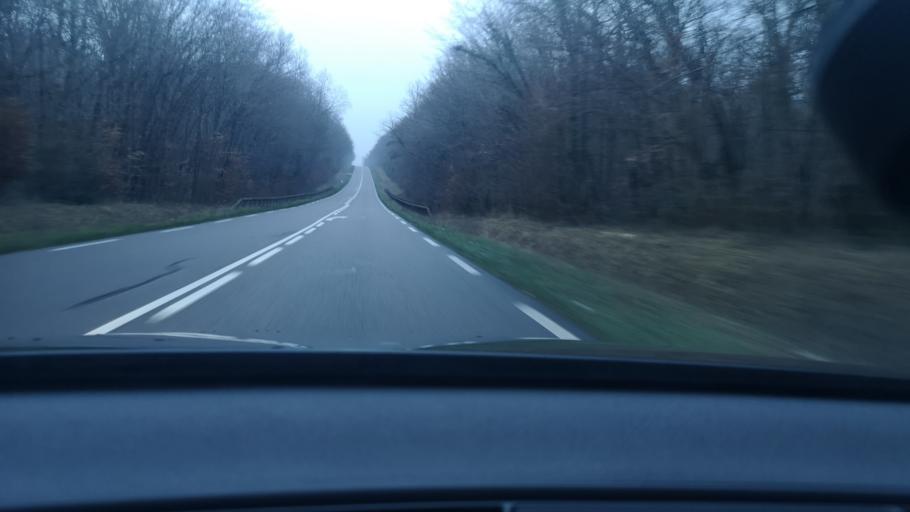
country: FR
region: Bourgogne
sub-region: Departement de la Cote-d'Or
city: Aiserey
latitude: 47.1015
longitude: 5.1030
